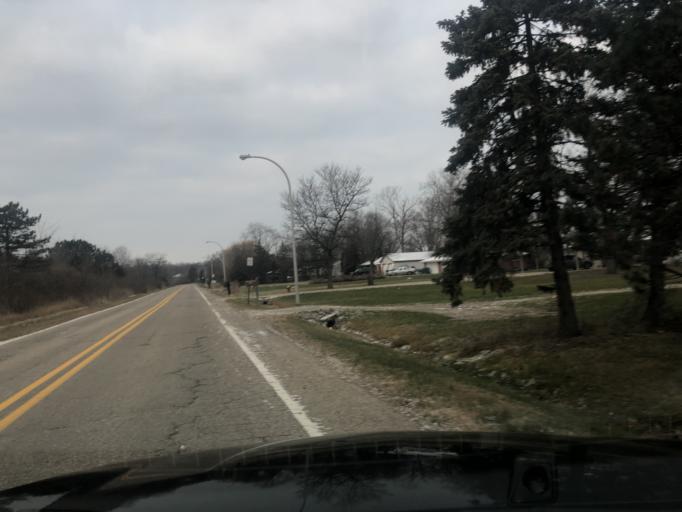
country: US
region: Michigan
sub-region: Wayne County
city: Romulus
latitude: 42.2305
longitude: -83.3806
